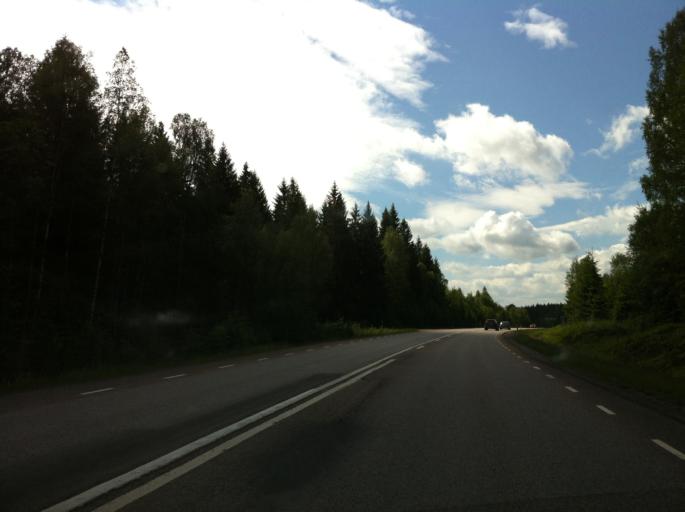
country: SE
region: Vaermland
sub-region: Grums Kommun
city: Slottsbron
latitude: 59.2448
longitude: 13.0045
